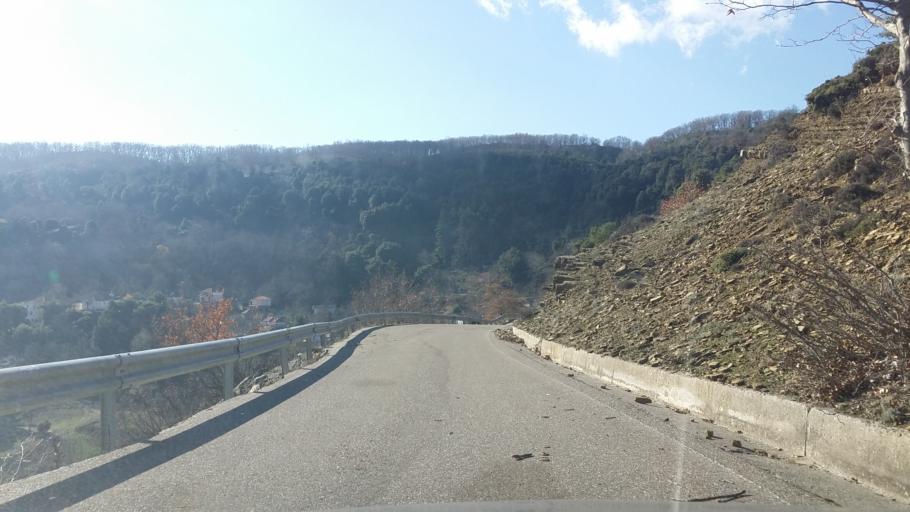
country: GR
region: West Greece
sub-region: Nomos Aitolias kai Akarnanias
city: Krikellos
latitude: 39.0120
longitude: 21.2717
